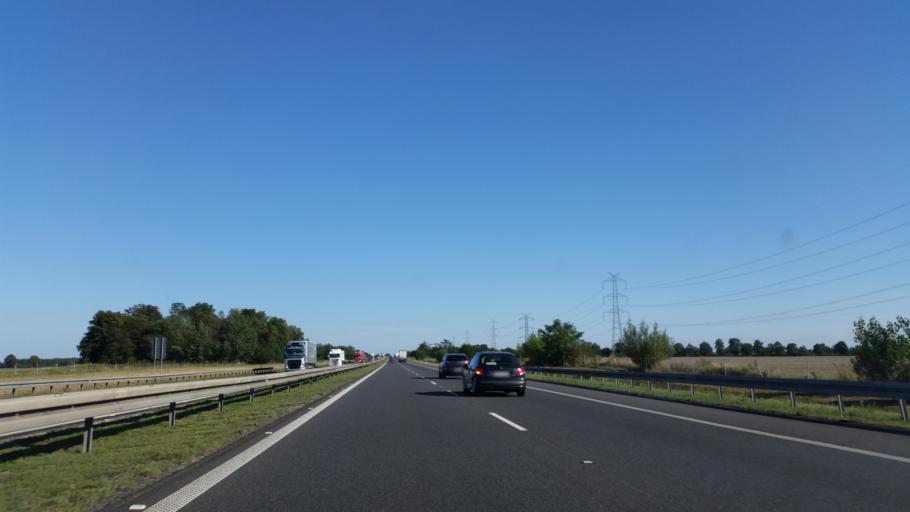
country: PL
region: Lower Silesian Voivodeship
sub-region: Powiat strzelinski
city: Wiazow
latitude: 50.8318
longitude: 17.2880
